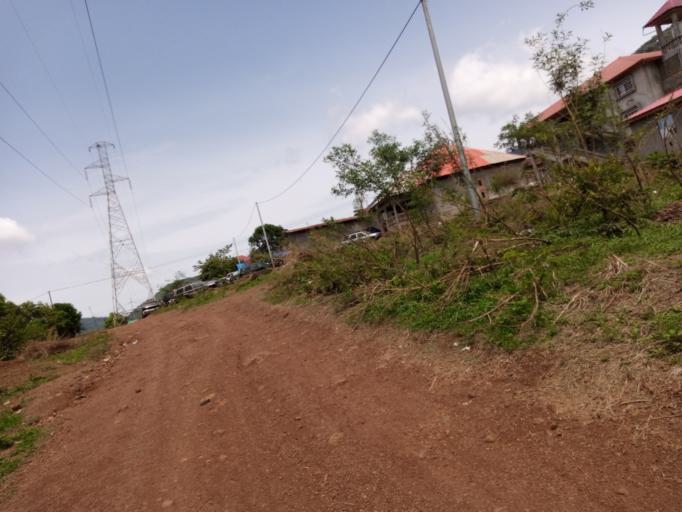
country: SL
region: Western Area
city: Hastings
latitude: 8.3735
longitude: -13.1359
